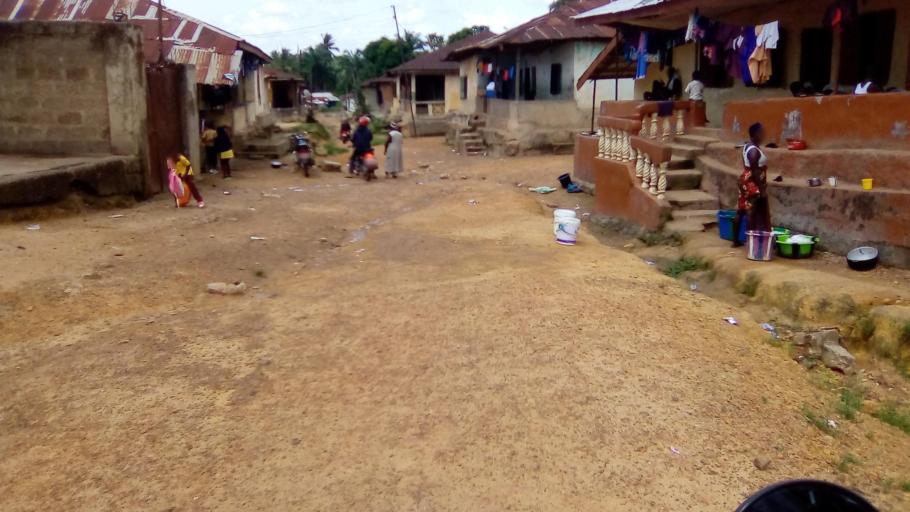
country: SL
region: Southern Province
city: Bo
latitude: 7.9633
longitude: -11.7295
